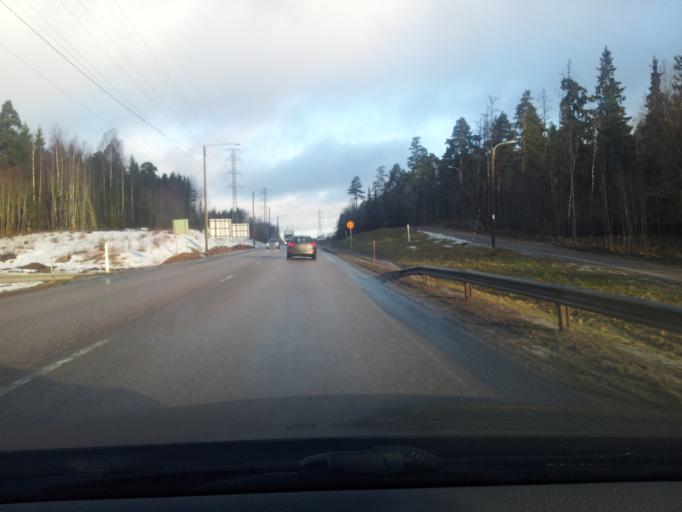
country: FI
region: Uusimaa
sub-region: Helsinki
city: Espoo
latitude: 60.1767
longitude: 24.6121
